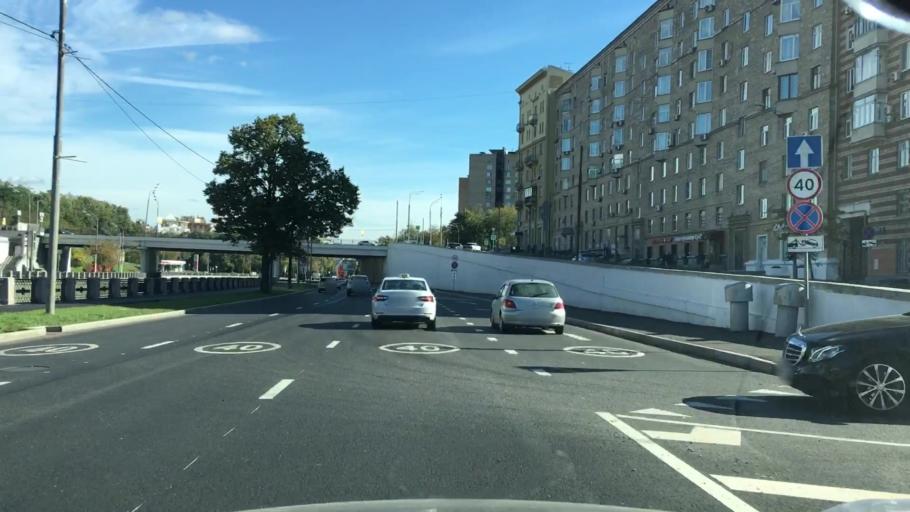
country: RU
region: Moscow
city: Taganskiy
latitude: 55.7495
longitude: 37.6526
